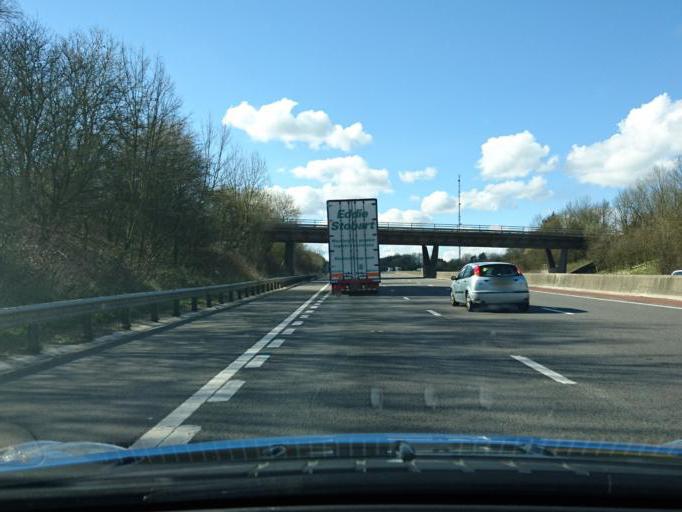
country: GB
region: England
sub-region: West Berkshire
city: Lambourn
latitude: 51.4788
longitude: -1.5502
